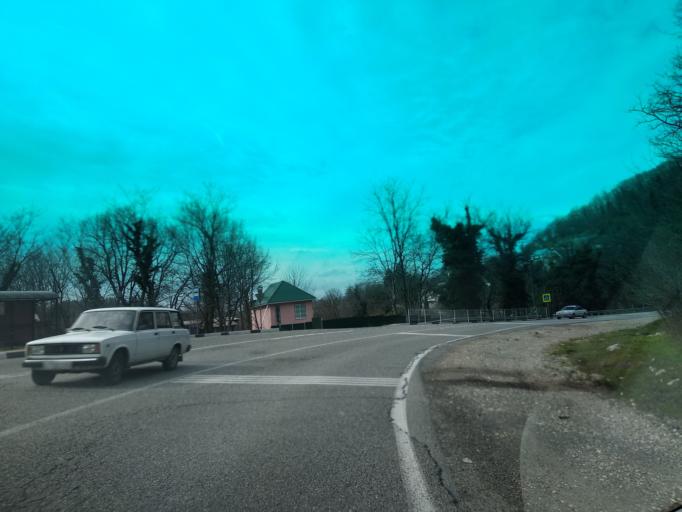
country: RU
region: Krasnodarskiy
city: Shepsi
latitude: 44.0810
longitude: 39.1332
